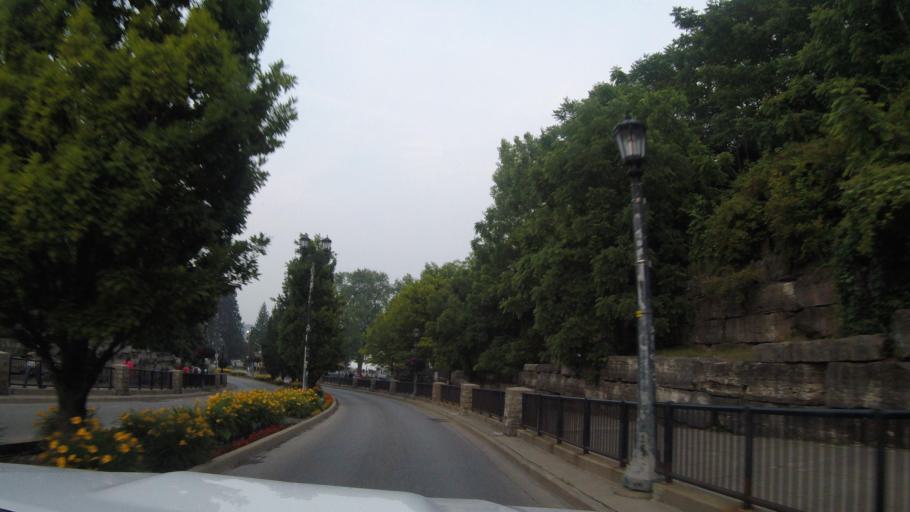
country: CA
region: Ontario
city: Niagara Falls
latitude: 43.0837
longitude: -79.0797
